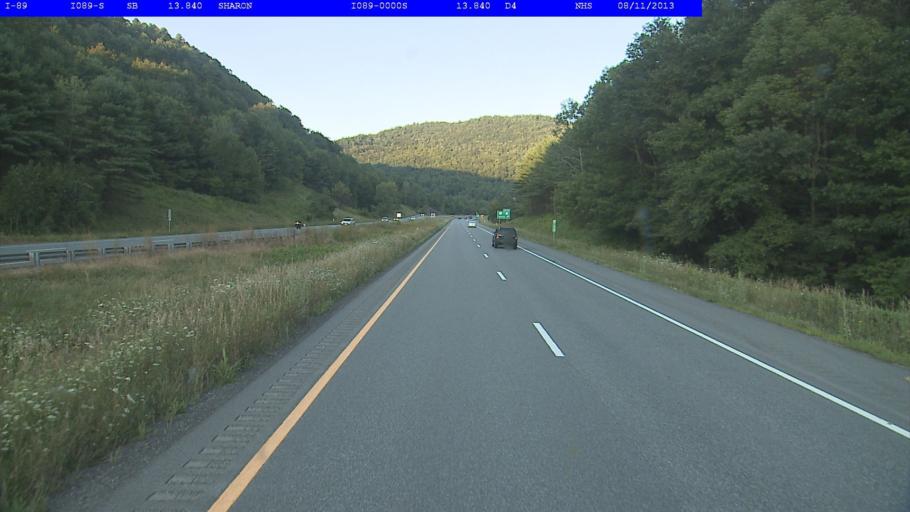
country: US
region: Vermont
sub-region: Windsor County
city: Woodstock
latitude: 43.7850
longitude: -72.4602
